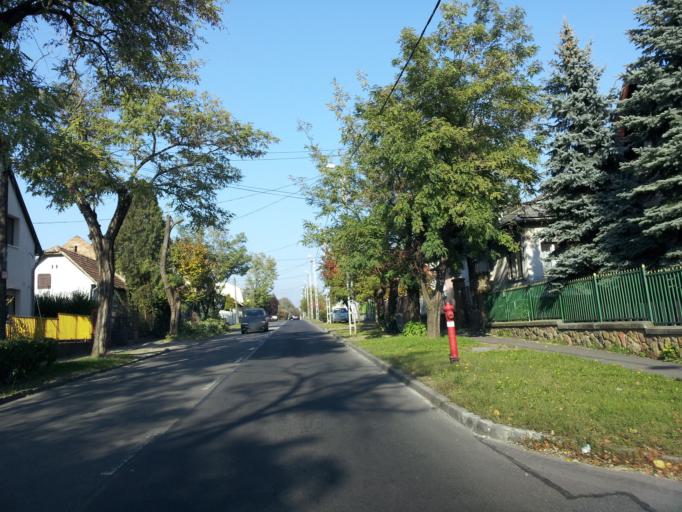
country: HU
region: Budapest
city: Budapest XVIII. keruelet
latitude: 47.4601
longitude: 19.1774
